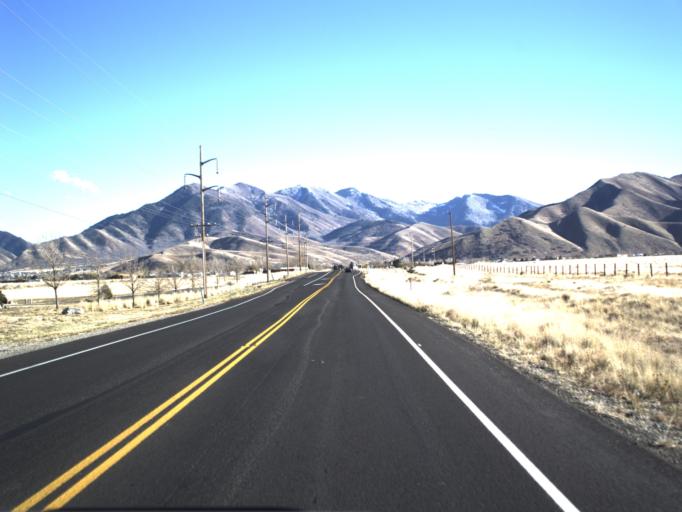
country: US
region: Utah
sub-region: Tooele County
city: Tooele
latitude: 40.5396
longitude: -112.3335
